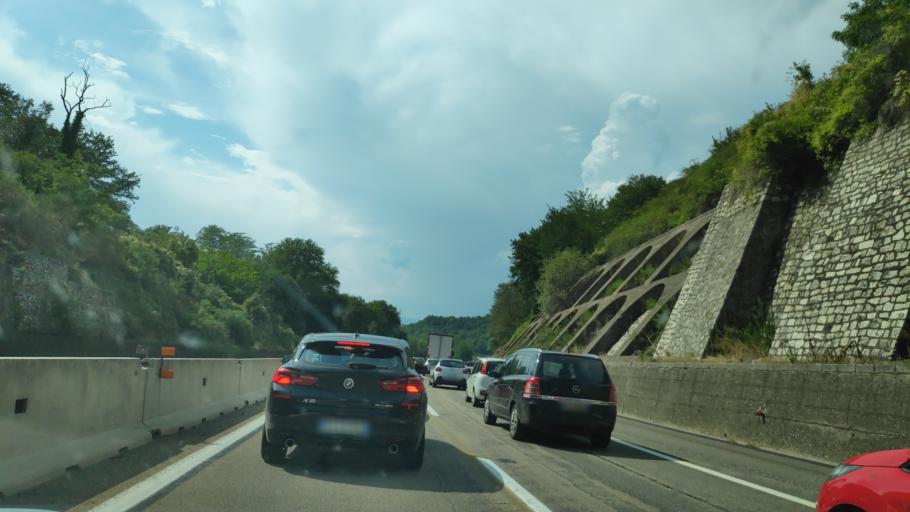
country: IT
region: Tuscany
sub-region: Province of Arezzo
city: Montalto
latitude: 43.5132
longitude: 11.6403
